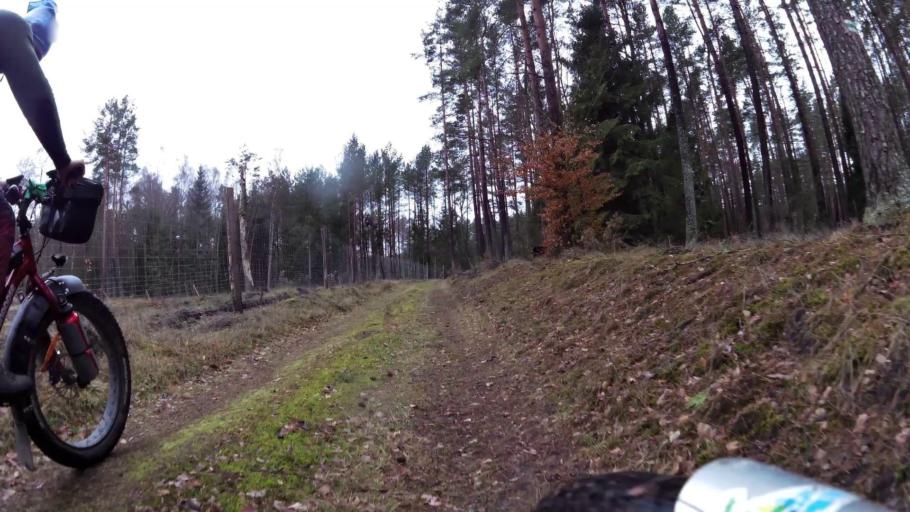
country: PL
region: Pomeranian Voivodeship
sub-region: Powiat bytowski
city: Borzytuchom
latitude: 54.2636
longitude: 17.3437
